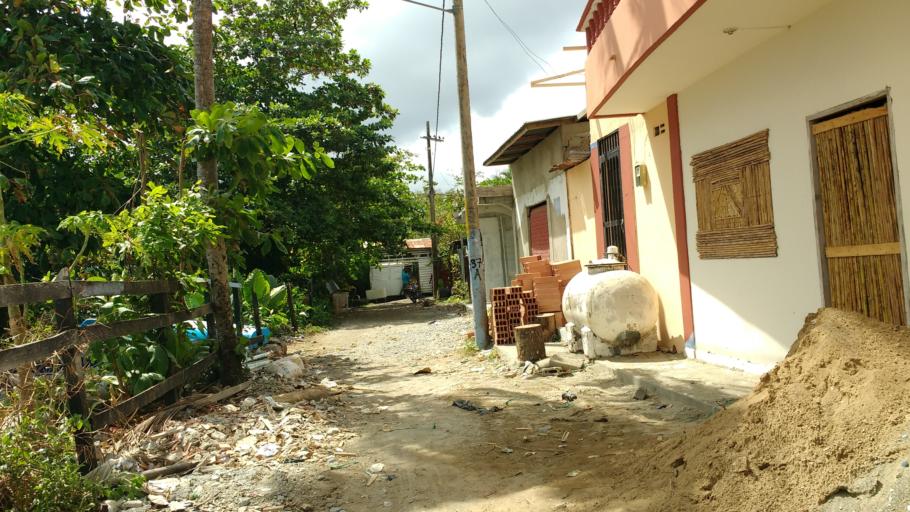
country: PA
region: Guna Yala
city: Puerto Obaldia
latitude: 8.6355
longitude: -77.3472
